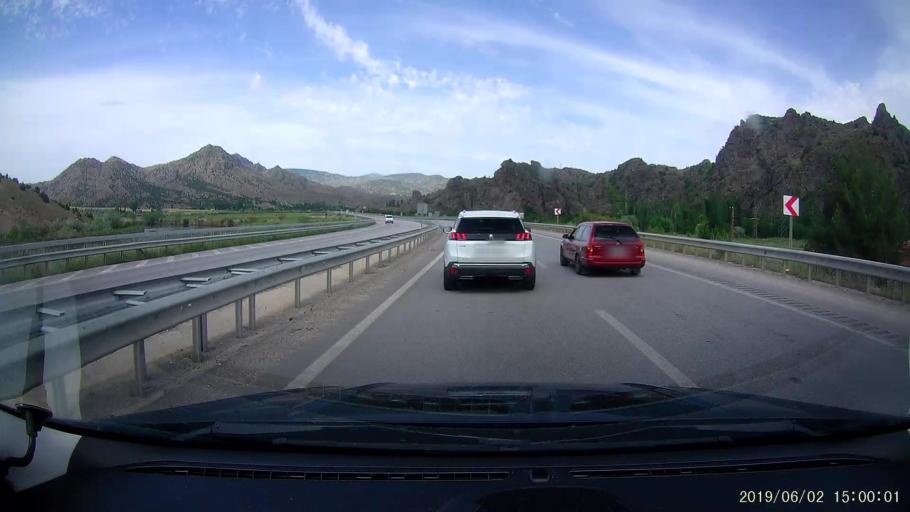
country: TR
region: Corum
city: Osmancik
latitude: 40.9730
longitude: 34.7058
